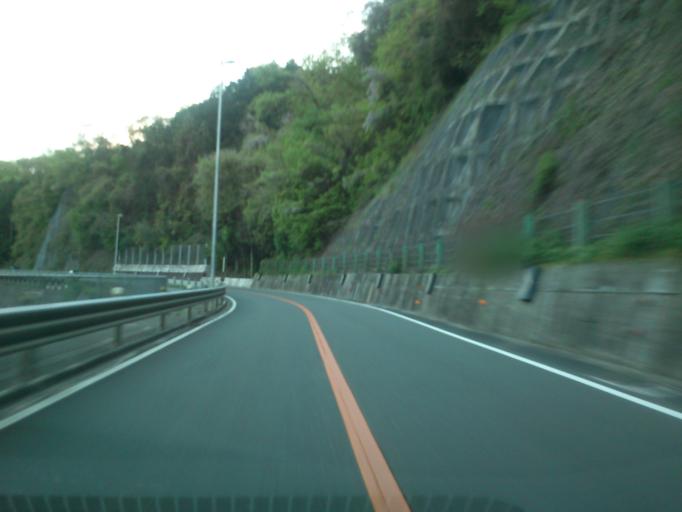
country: JP
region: Kyoto
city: Ayabe
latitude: 35.2039
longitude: 135.4221
